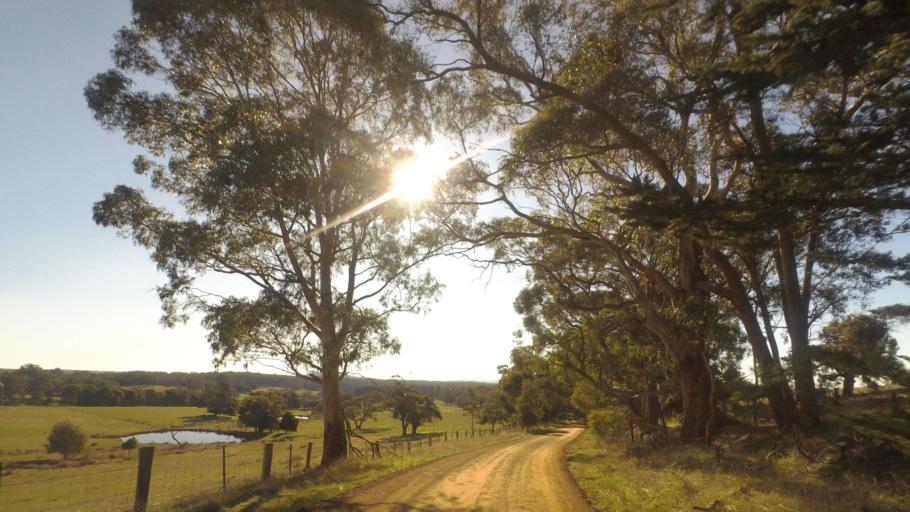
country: AU
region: Victoria
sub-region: Mount Alexander
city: Castlemaine
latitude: -37.3001
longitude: 144.3335
